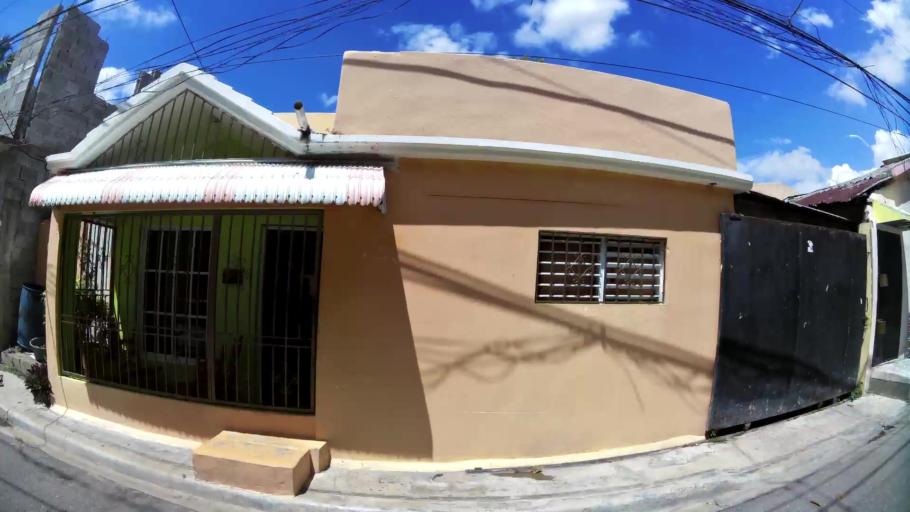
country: DO
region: Santiago
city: Santiago de los Caballeros
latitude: 19.4610
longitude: -70.6662
